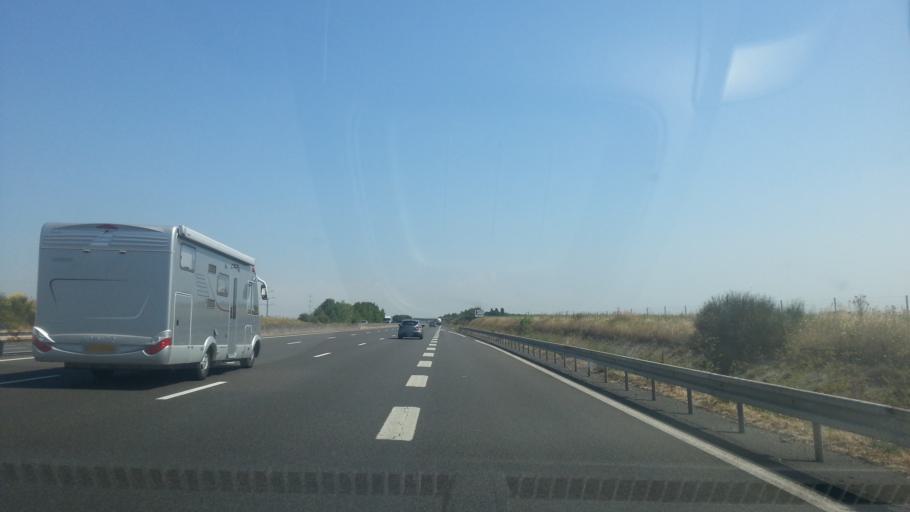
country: FR
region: Centre
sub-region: Departement du Loiret
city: Baule
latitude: 47.8222
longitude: 1.6461
